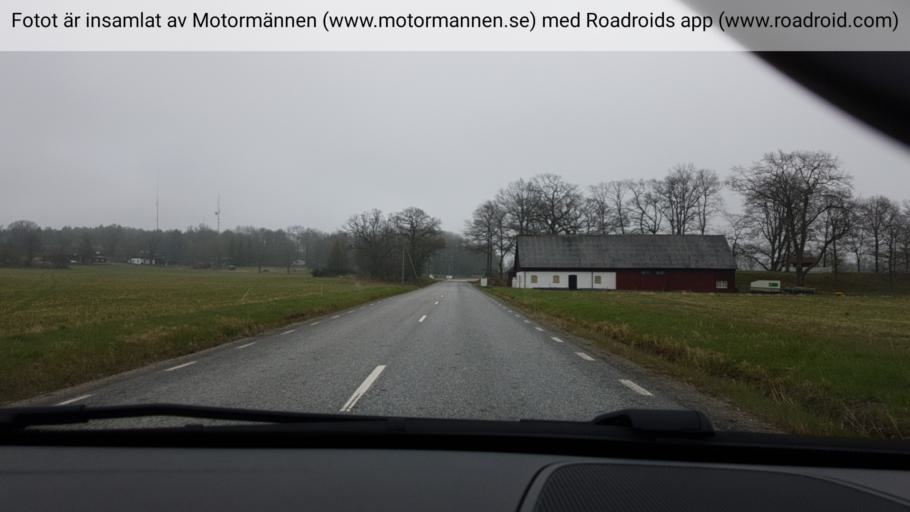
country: SE
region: Stockholm
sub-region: Haninge Kommun
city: Jordbro
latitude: 59.0040
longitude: 18.1165
